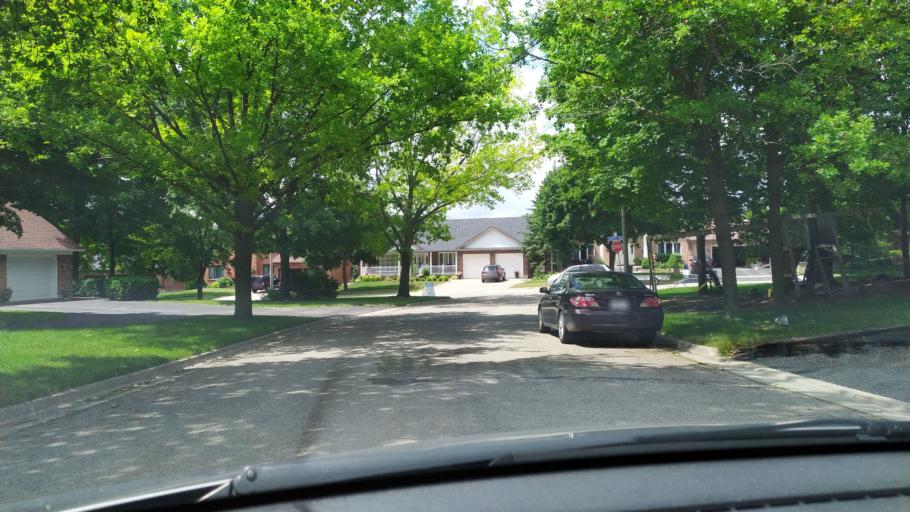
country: CA
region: Ontario
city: Kitchener
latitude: 43.4448
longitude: -80.4310
